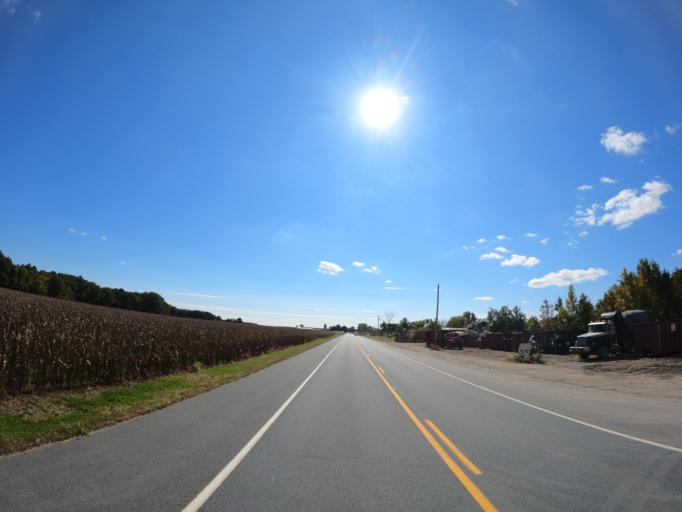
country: US
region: Delaware
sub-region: Sussex County
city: Bridgeville
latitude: 38.8169
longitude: -75.6188
